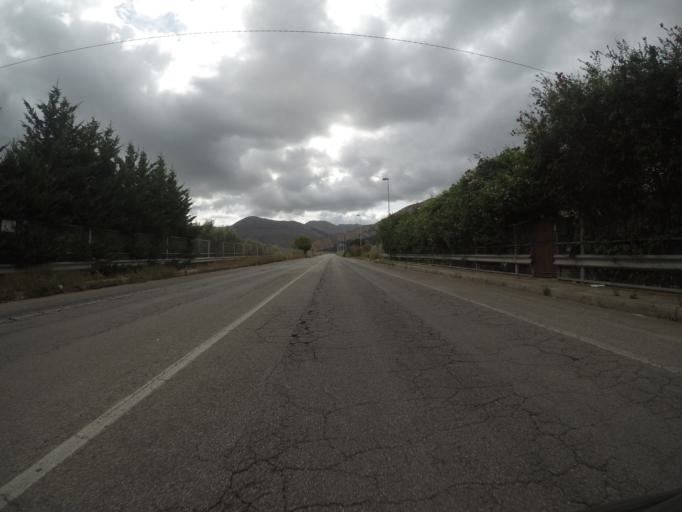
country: IT
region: Sicily
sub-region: Palermo
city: Capaci
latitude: 38.1703
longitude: 13.2206
